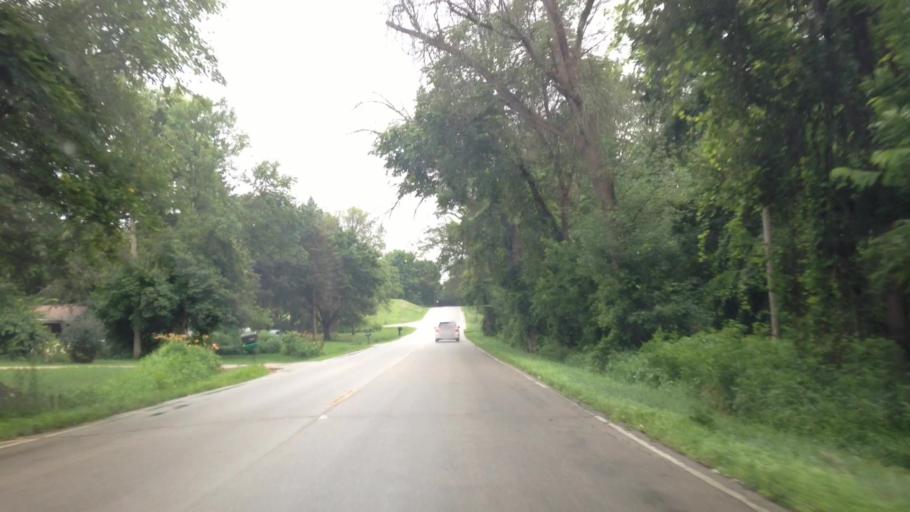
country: US
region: Wisconsin
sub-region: Waukesha County
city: Lannon
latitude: 43.1905
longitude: -88.1824
